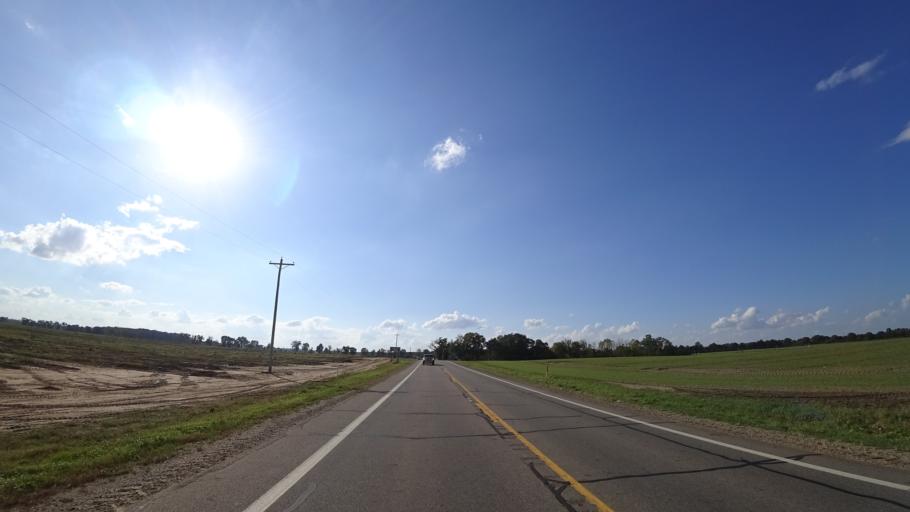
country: US
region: Michigan
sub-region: Saint Joseph County
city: Centreville
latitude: 41.9258
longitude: -85.5678
